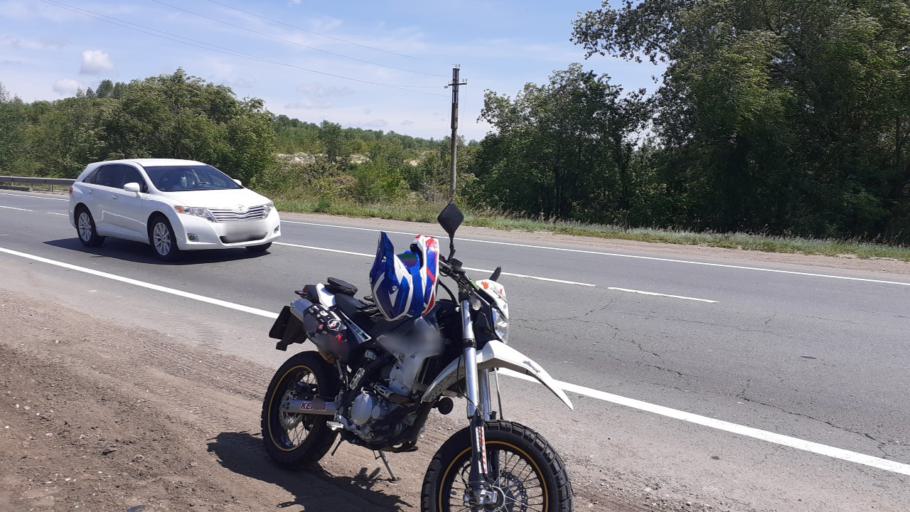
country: RU
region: Samara
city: Chapayevsk
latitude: 52.9278
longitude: 49.7062
